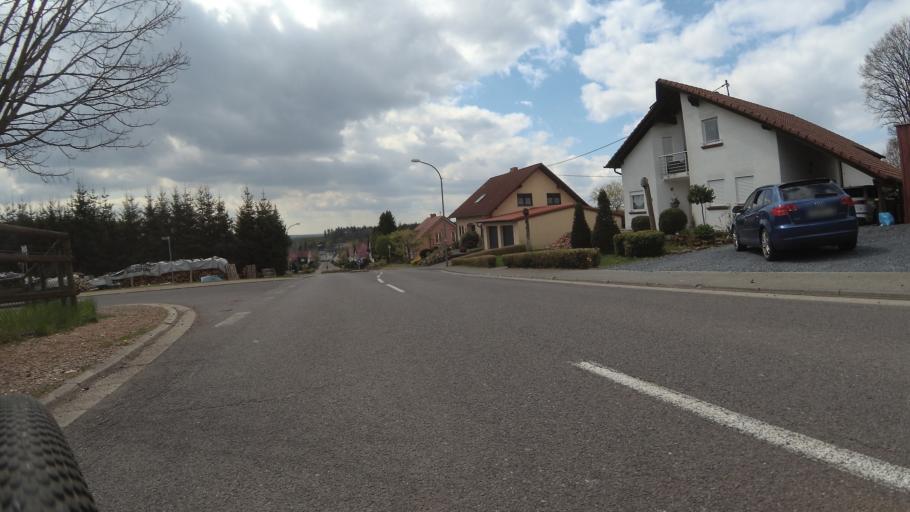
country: DE
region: Saarland
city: Britten
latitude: 49.5268
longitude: 6.6706
